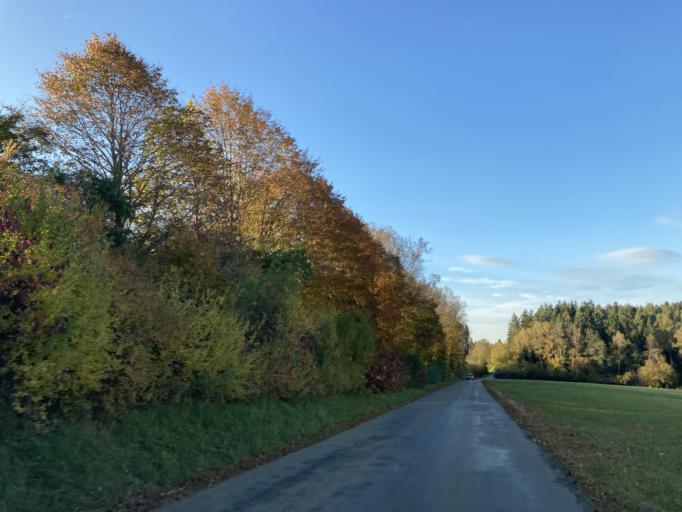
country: DE
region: Baden-Wuerttemberg
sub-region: Freiburg Region
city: Villingen-Schwenningen
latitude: 48.0164
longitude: 8.4529
